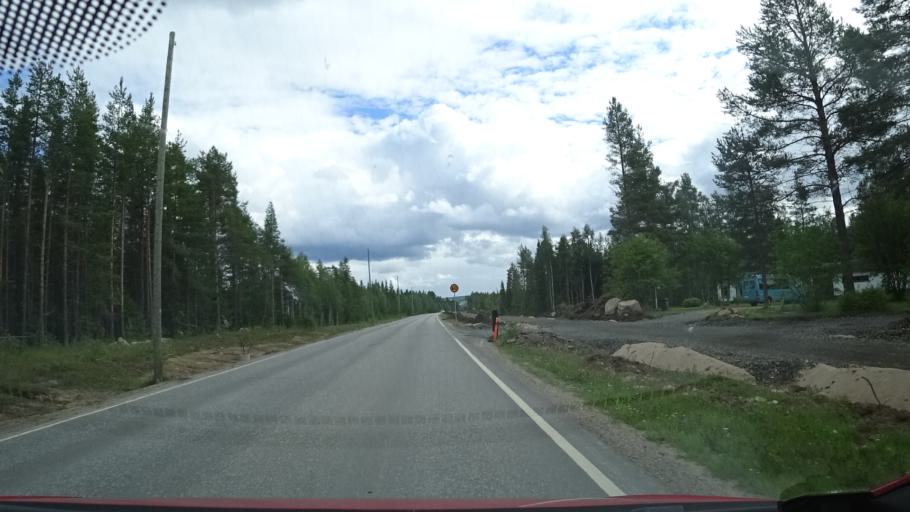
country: FI
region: Lapland
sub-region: Rovaniemi
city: Rovaniemi
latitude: 66.5367
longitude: 25.7261
